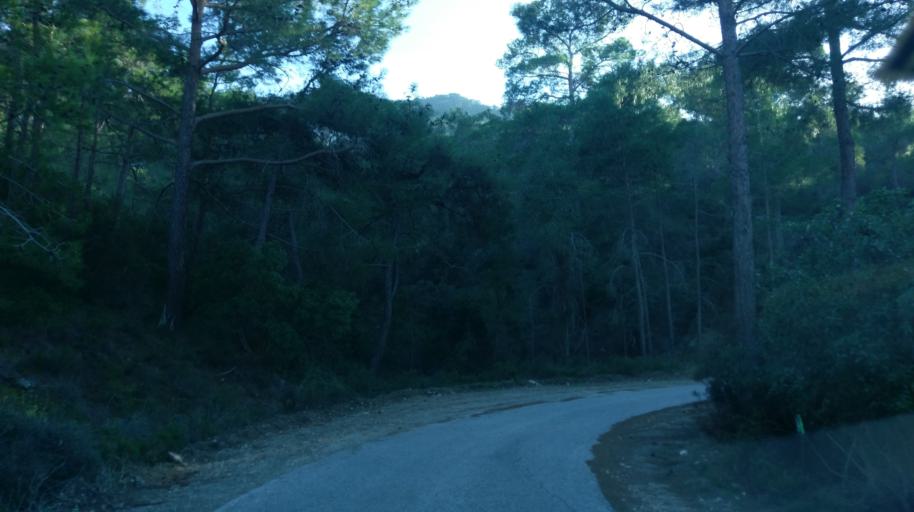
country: CY
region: Ammochostos
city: Lefkonoiko
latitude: 35.3218
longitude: 33.5931
